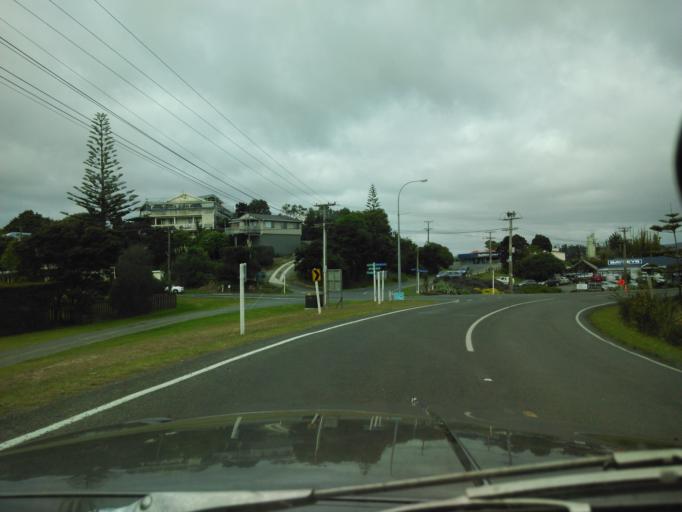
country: NZ
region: Auckland
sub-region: Auckland
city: Wellsford
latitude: -36.0997
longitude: 174.5882
